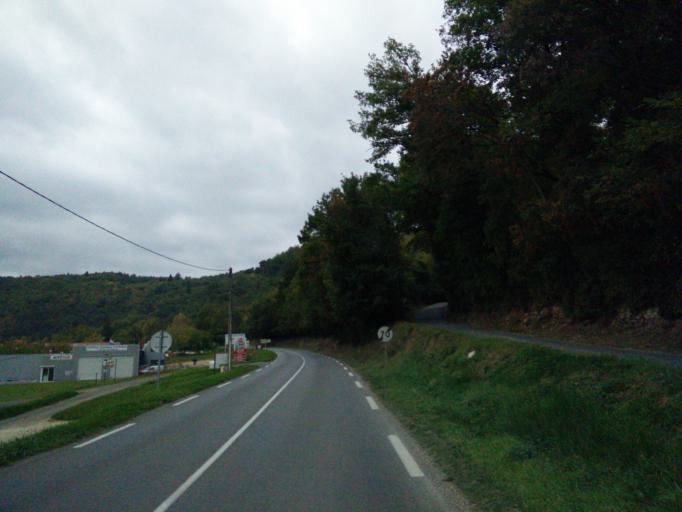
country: FR
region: Midi-Pyrenees
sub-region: Departement du Lot
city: Prayssac
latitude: 44.5063
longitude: 1.1731
